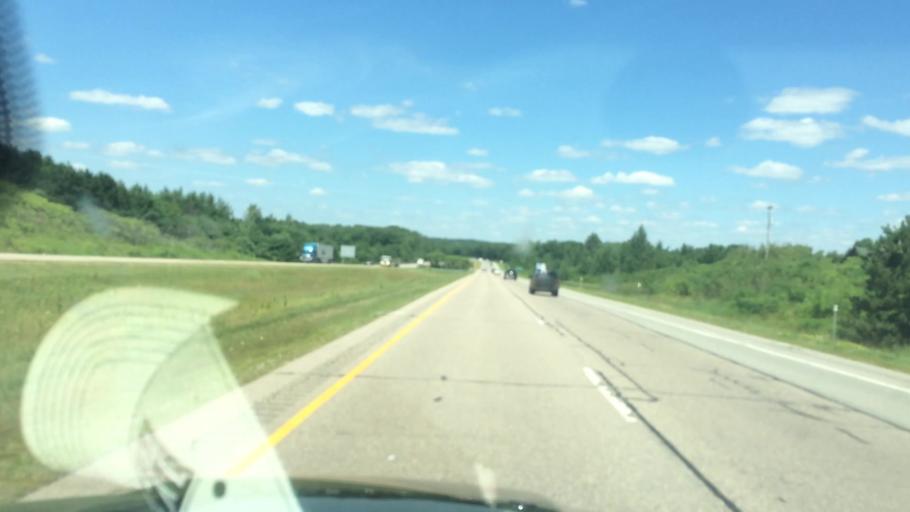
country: US
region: Wisconsin
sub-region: Marathon County
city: Mosinee
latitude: 44.6807
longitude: -89.6413
